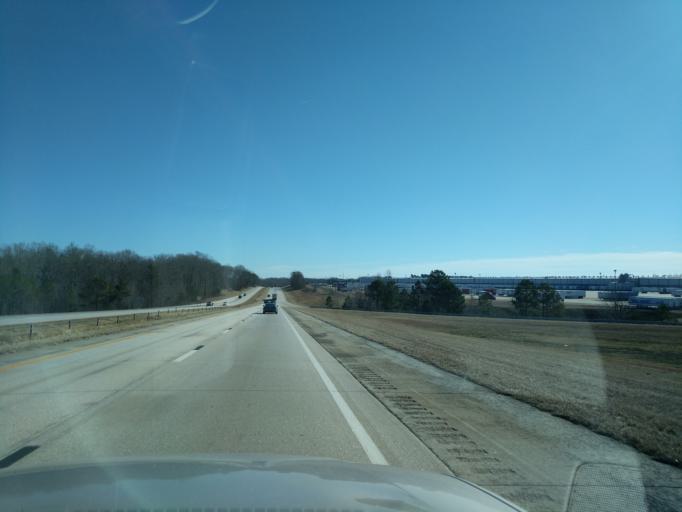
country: US
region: South Carolina
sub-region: Laurens County
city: Watts Mills
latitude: 34.5528
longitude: -82.0038
